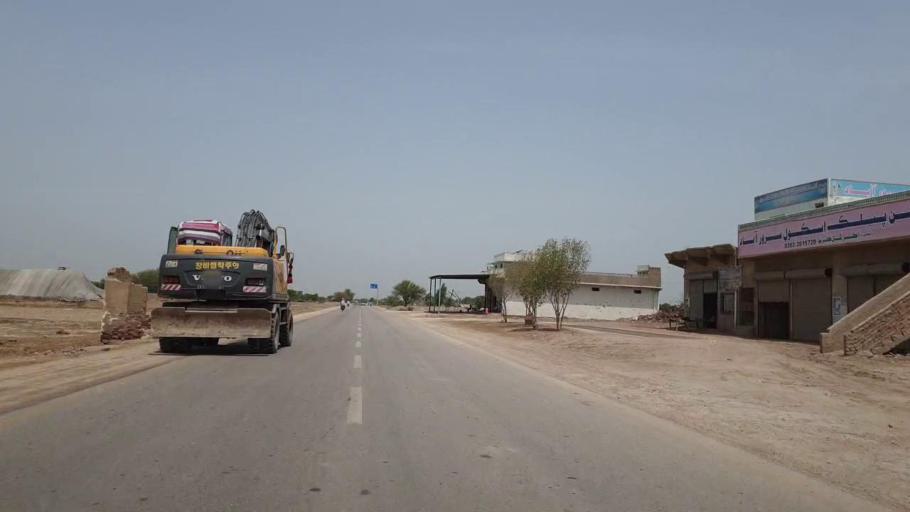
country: PK
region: Sindh
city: Shahpur Chakar
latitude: 26.1889
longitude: 68.5820
